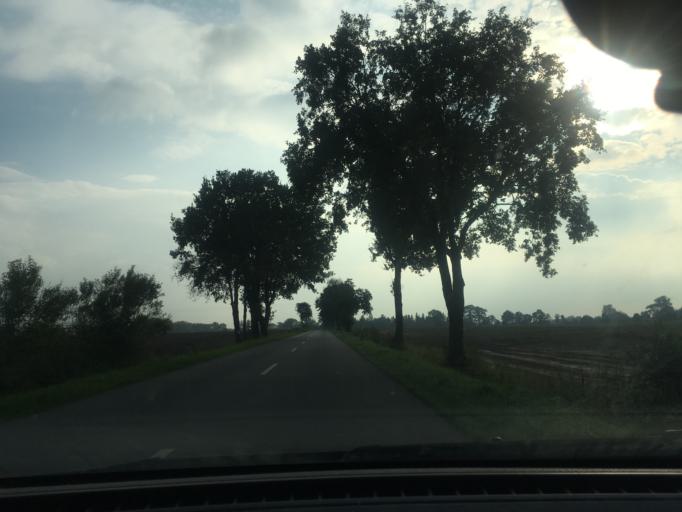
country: DE
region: Lower Saxony
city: Vastorf
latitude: 53.2111
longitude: 10.5505
